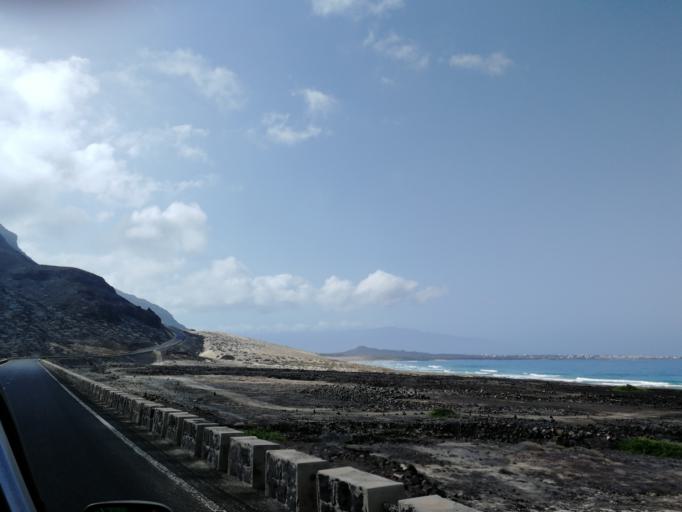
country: CV
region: Sao Vicente
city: Mindelo
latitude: 16.8704
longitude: -24.9032
